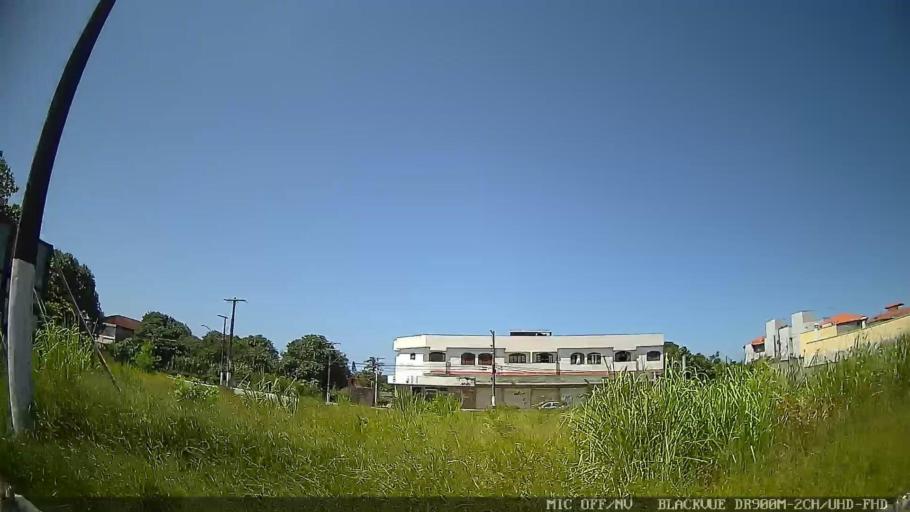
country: BR
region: Sao Paulo
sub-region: Peruibe
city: Peruibe
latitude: -24.3273
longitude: -47.0031
